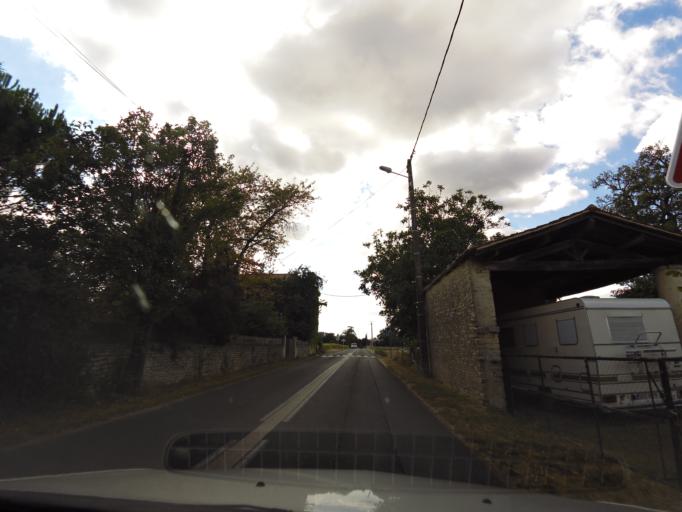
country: FR
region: Poitou-Charentes
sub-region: Departement des Deux-Sevres
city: Beauvoir-sur-Niort
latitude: 46.1480
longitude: -0.3949
